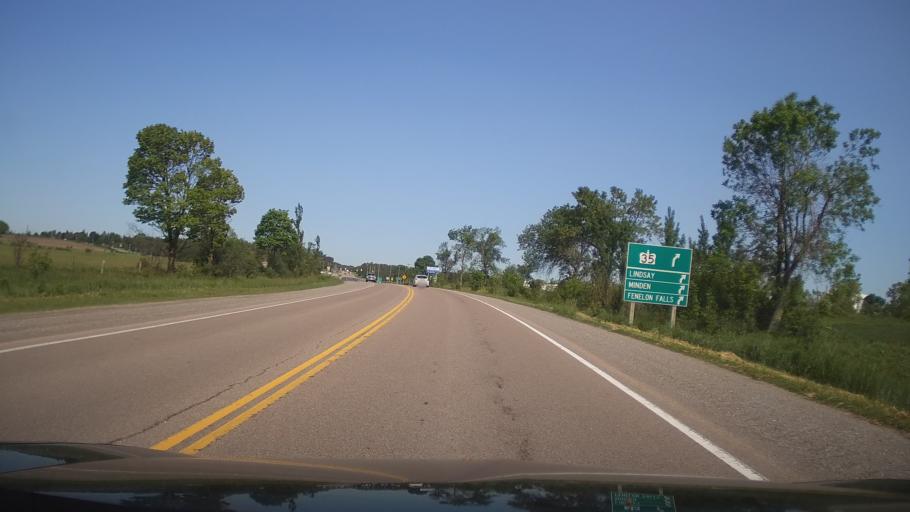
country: CA
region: Ontario
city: Omemee
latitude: 44.3444
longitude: -78.7691
